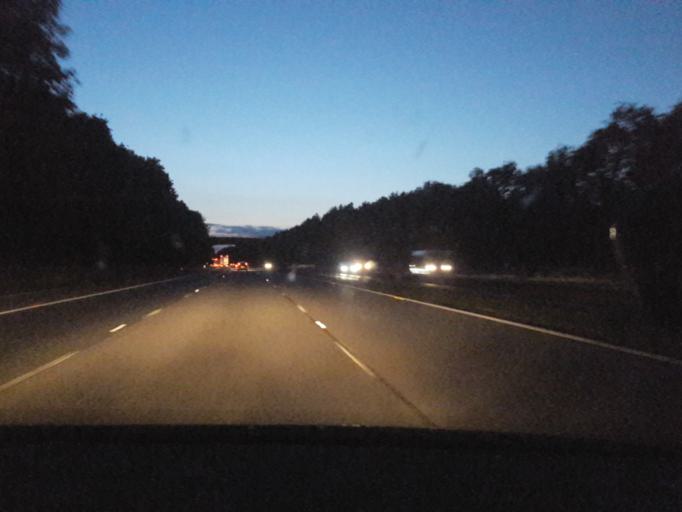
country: GB
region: England
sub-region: Leicestershire
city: Kirby Muxloe
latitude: 52.6549
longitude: -1.2444
